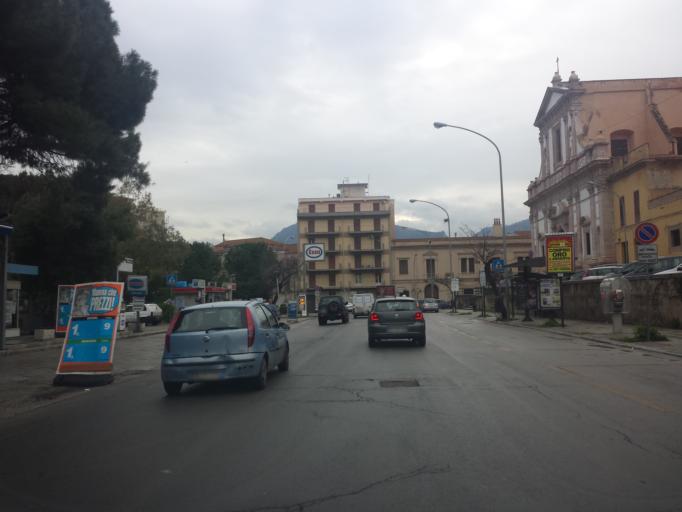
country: IT
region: Sicily
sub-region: Palermo
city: Palermo
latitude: 38.1106
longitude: 13.3501
